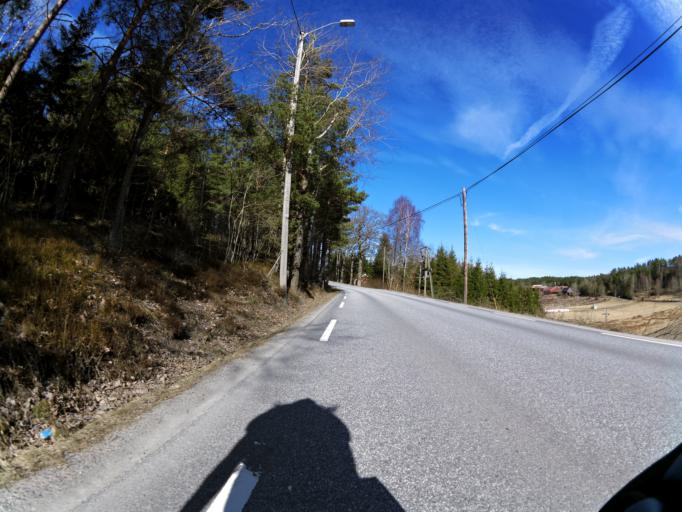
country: NO
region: Ostfold
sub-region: Fredrikstad
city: Fredrikstad
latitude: 59.2633
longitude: 10.9429
